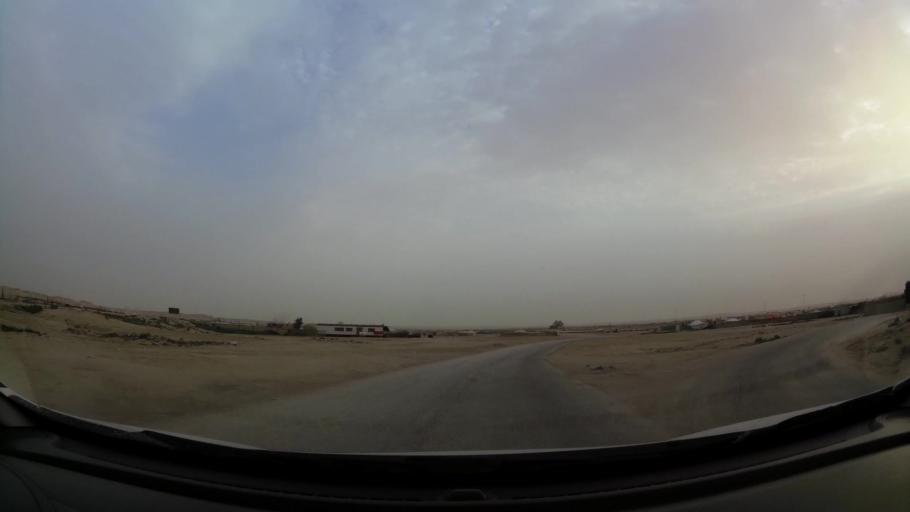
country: BH
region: Central Governorate
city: Dar Kulayb
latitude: 26.0001
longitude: 50.5852
